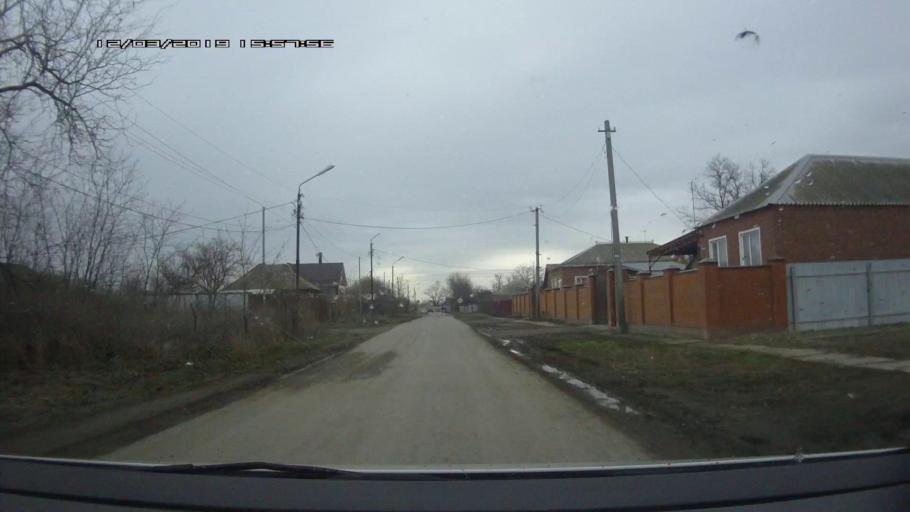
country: RU
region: Rostov
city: Novobataysk
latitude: 46.9027
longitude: 39.7877
